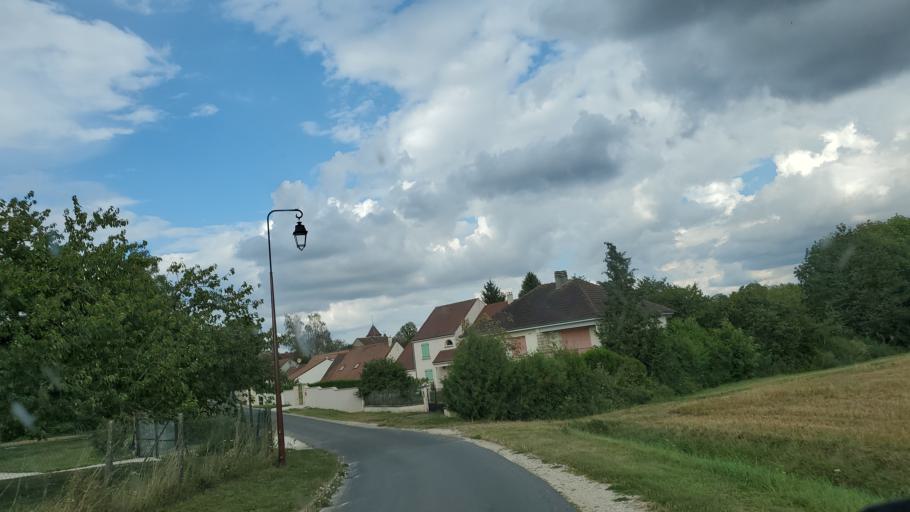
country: FR
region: Ile-de-France
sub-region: Departement de Seine-et-Marne
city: Chailly-en-Brie
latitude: 48.7745
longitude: 3.1617
